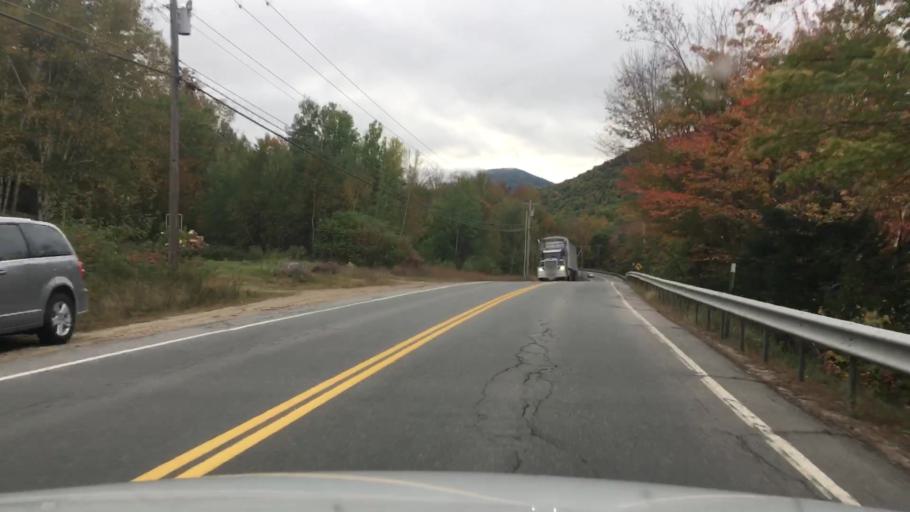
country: US
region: New Hampshire
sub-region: Carroll County
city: North Conway
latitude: 44.1863
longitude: -71.2274
